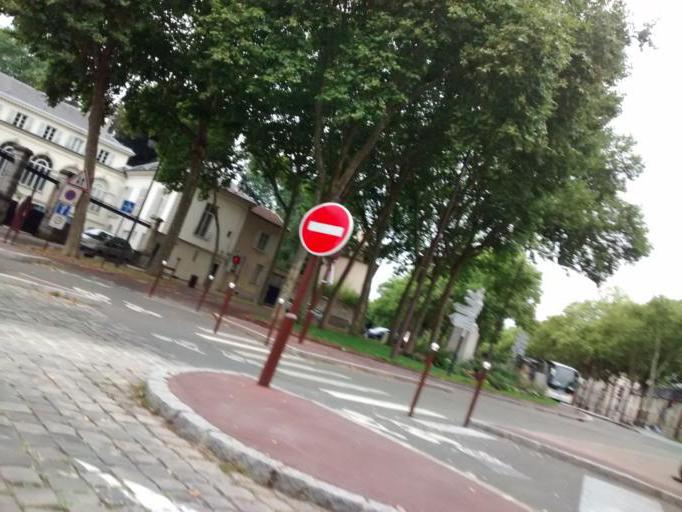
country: FR
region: Ile-de-France
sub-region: Departement des Yvelines
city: Versailles
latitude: 48.8055
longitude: 2.1416
